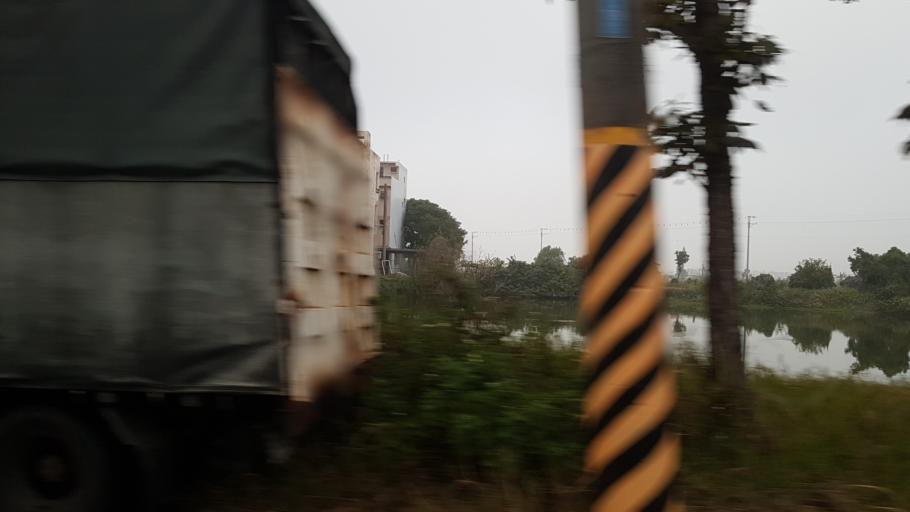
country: TW
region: Taiwan
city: Xinying
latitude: 23.3416
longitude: 120.3296
